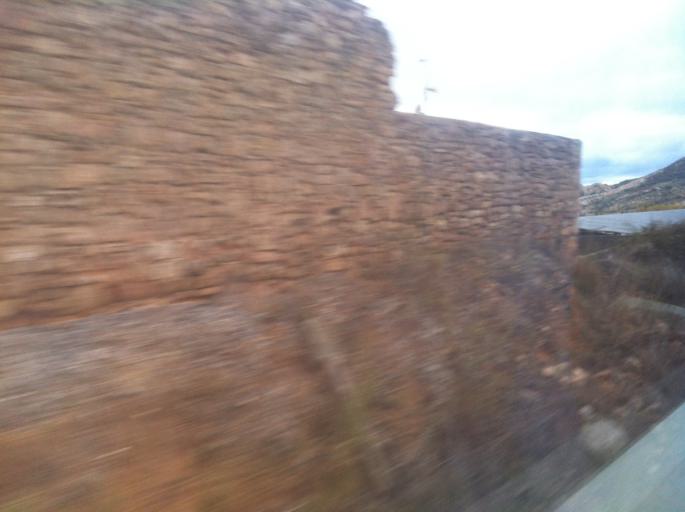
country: ES
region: Castille and Leon
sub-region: Provincia de Burgos
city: Bugedo
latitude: 42.6485
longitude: -3.0170
